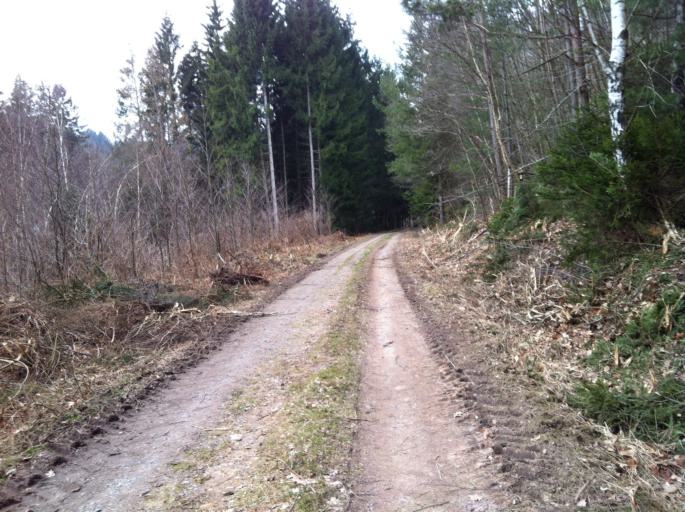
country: DE
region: Hesse
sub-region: Regierungsbezirk Darmstadt
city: Wald-Michelbach
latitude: 49.6270
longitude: 8.8995
